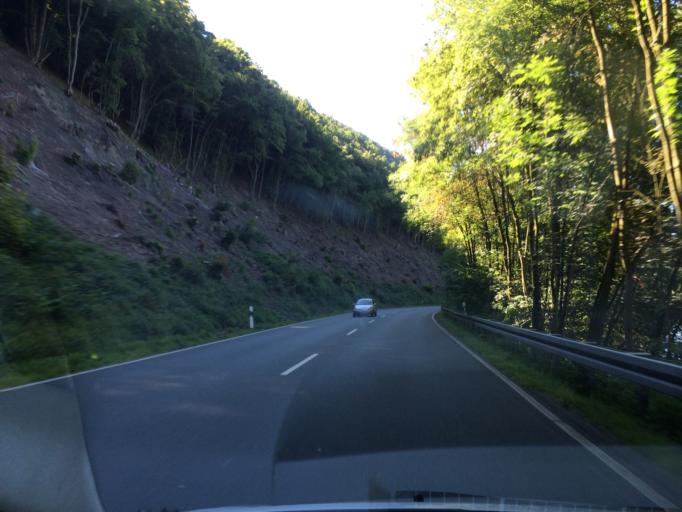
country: DE
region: North Rhine-Westphalia
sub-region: Regierungsbezirk Arnsberg
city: Nachrodt-Wiblingwerde
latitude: 51.3538
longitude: 7.6419
